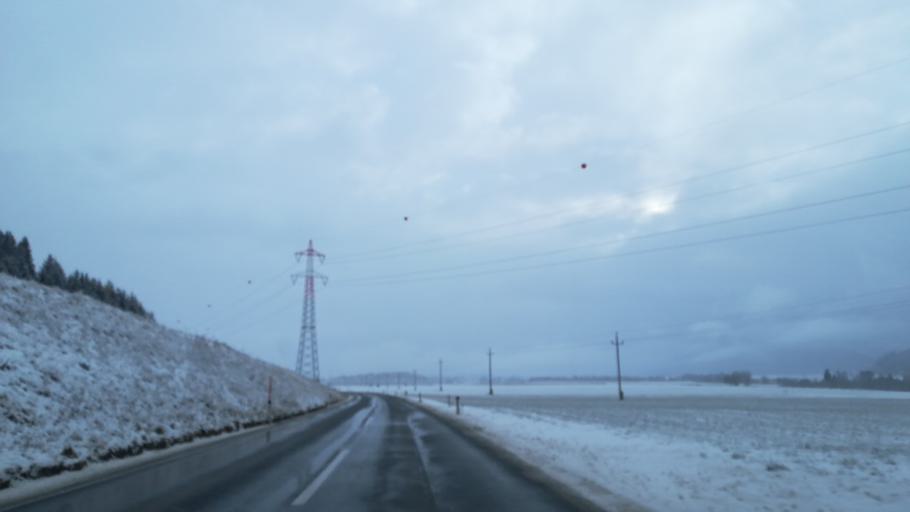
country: AT
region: Styria
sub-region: Politischer Bezirk Murtal
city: Poels
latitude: 47.2069
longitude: 14.6320
